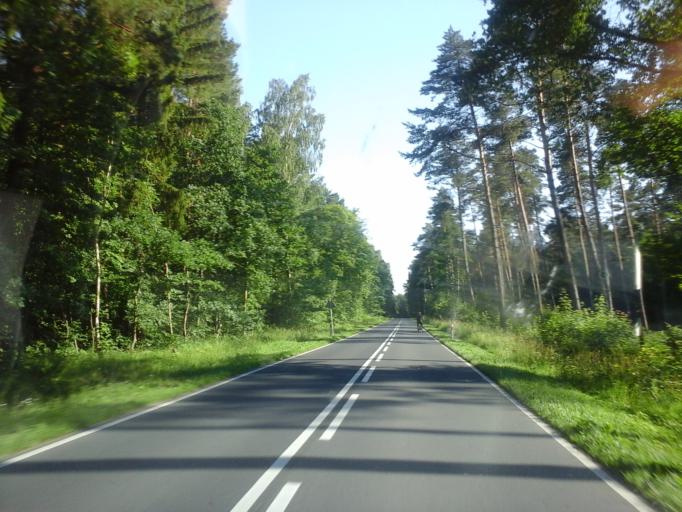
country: PL
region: West Pomeranian Voivodeship
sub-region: Powiat stargardzki
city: Chociwel
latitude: 53.4901
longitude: 15.3400
